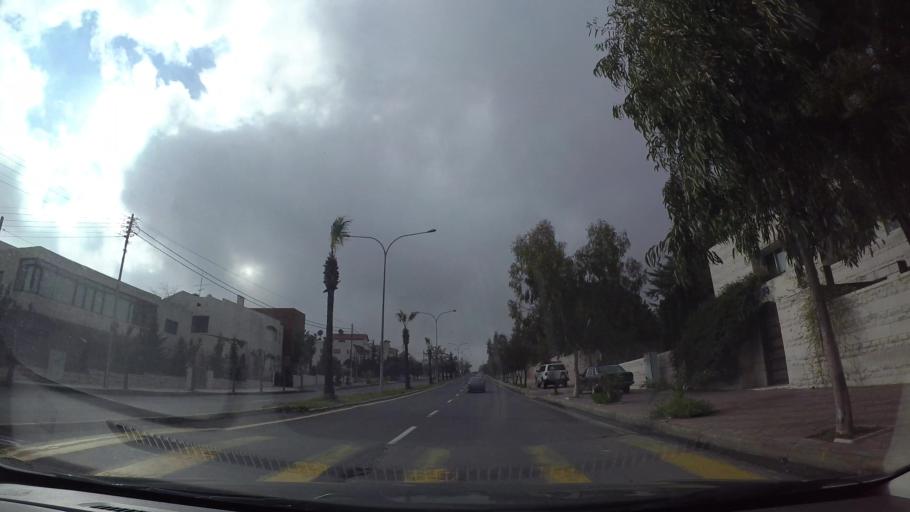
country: JO
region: Amman
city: Al Bunayyat ash Shamaliyah
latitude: 31.9509
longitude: 35.8868
